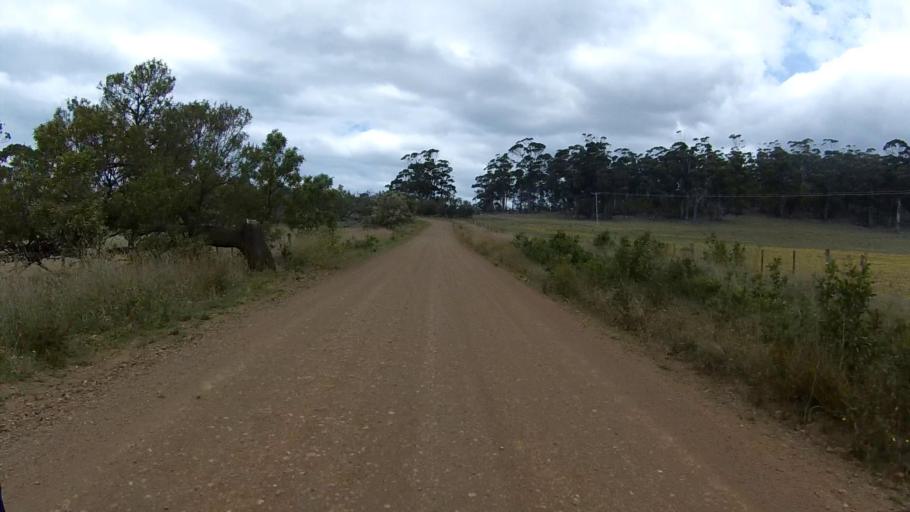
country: AU
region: Tasmania
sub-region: Sorell
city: Sorell
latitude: -42.6152
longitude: 147.9316
